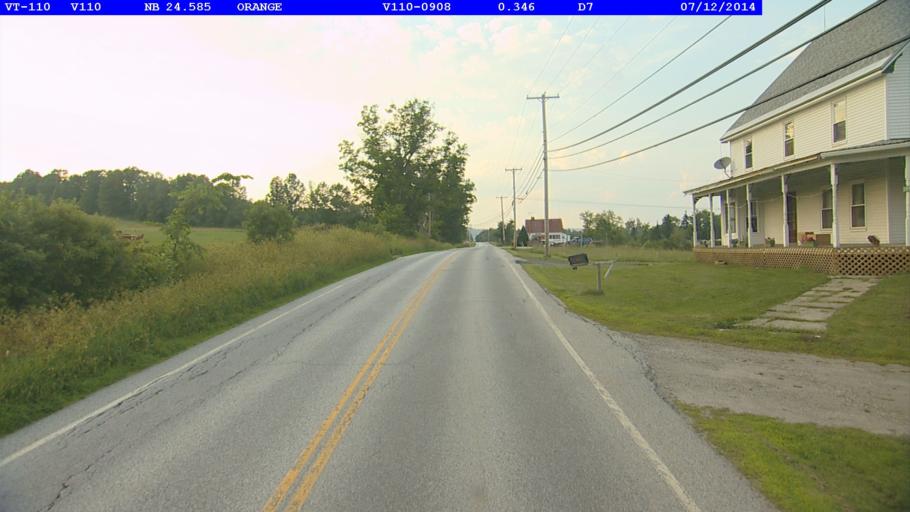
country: US
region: Vermont
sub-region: Washington County
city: South Barre
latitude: 44.1291
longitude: -72.4306
